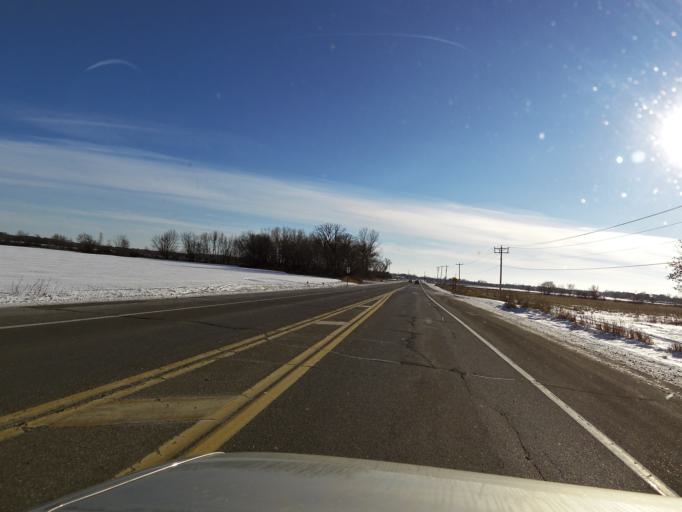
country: US
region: Minnesota
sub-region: Washington County
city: Lake Elmo
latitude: 45.0055
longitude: -92.8628
